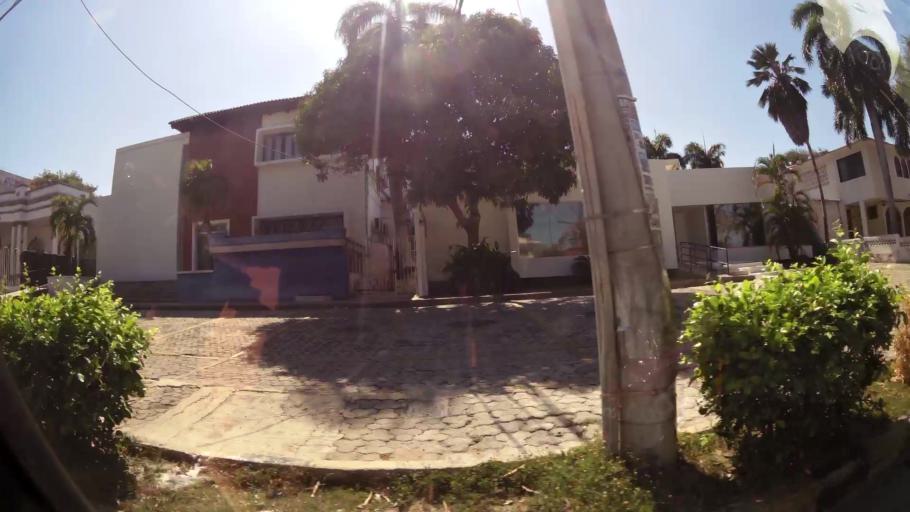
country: CO
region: Atlantico
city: Barranquilla
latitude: 11.0020
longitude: -74.7991
